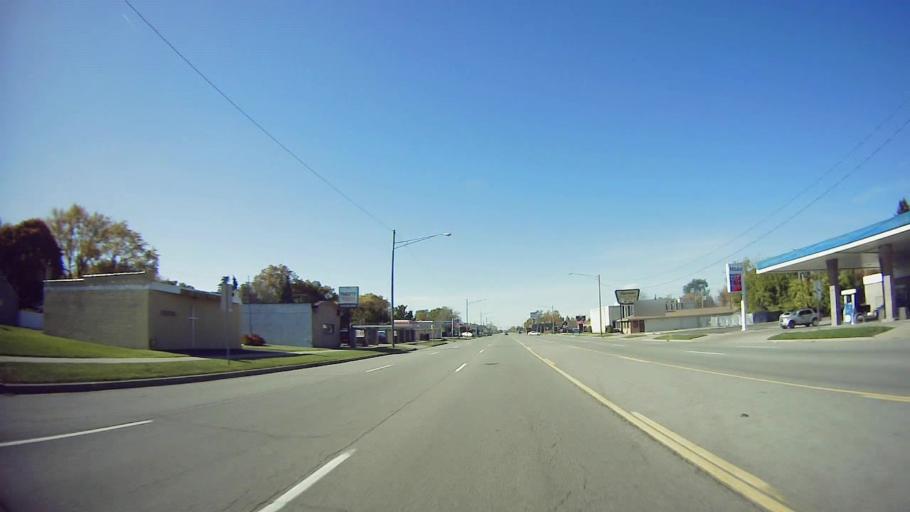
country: US
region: Michigan
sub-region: Wayne County
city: Redford
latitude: 42.3715
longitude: -83.2670
